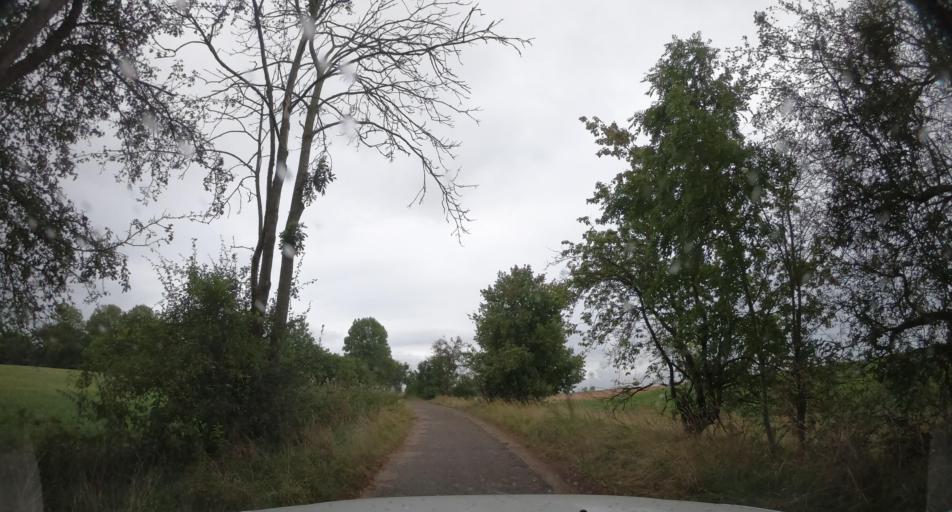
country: PL
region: West Pomeranian Voivodeship
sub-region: Powiat stargardzki
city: Suchan
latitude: 53.2744
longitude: 15.3948
